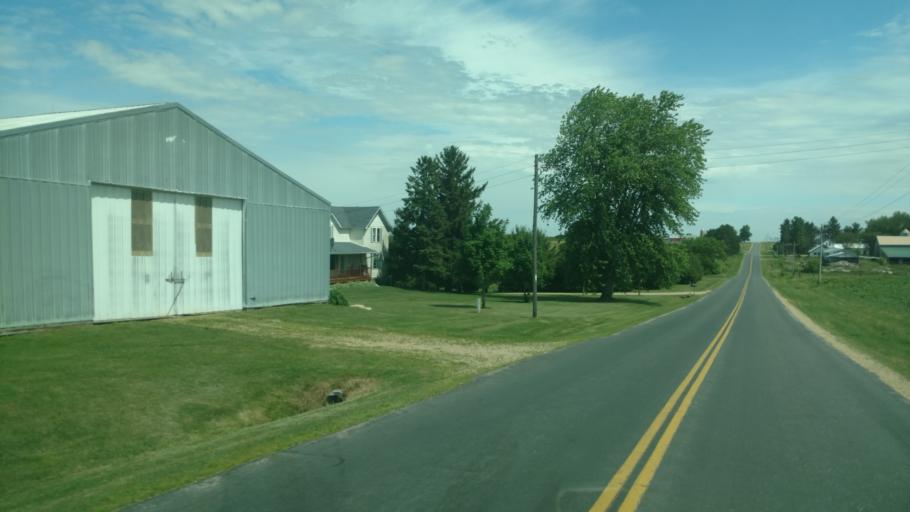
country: US
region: Wisconsin
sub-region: Vernon County
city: Hillsboro
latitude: 43.7534
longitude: -90.4330
